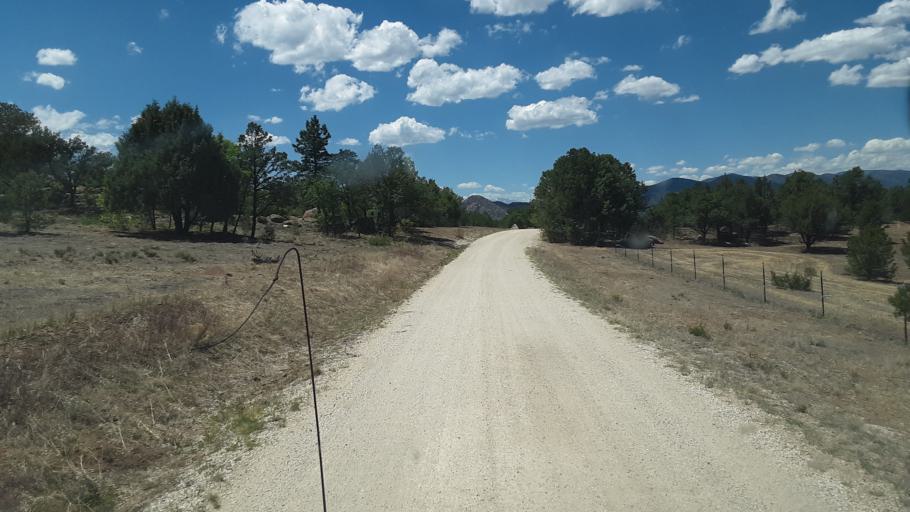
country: US
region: Colorado
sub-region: Custer County
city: Westcliffe
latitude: 38.3246
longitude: -105.6270
